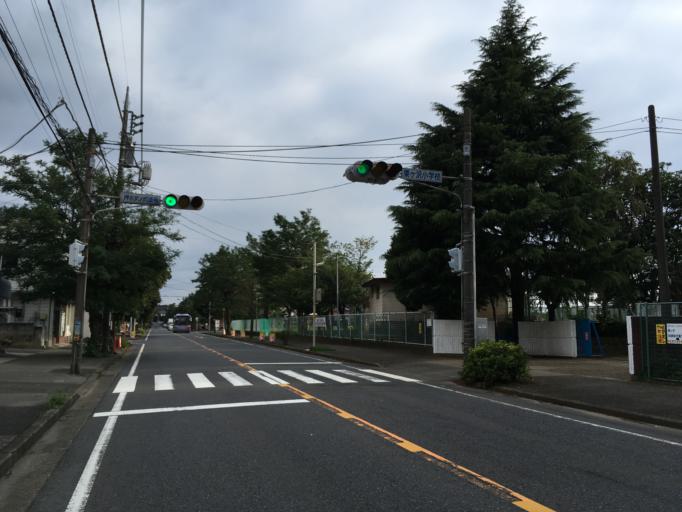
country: JP
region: Chiba
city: Kashiwa
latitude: 35.8160
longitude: 139.9494
